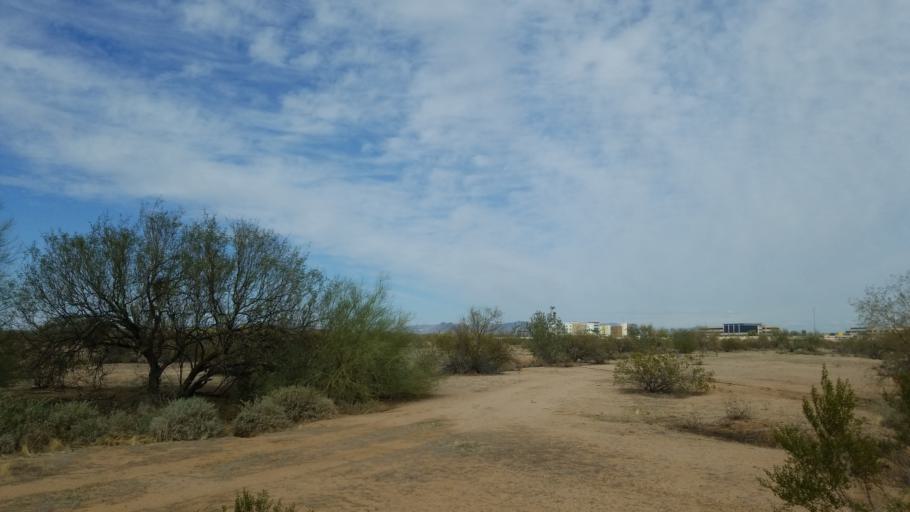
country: US
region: Arizona
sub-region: Maricopa County
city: Paradise Valley
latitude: 33.6677
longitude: -111.9861
